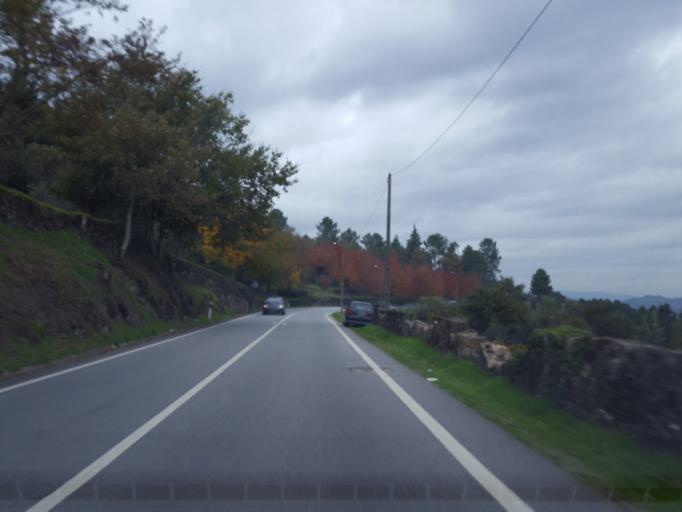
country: PT
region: Porto
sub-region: Marco de Canaveses
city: Marco de Canavezes
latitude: 41.1637
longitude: -8.1455
